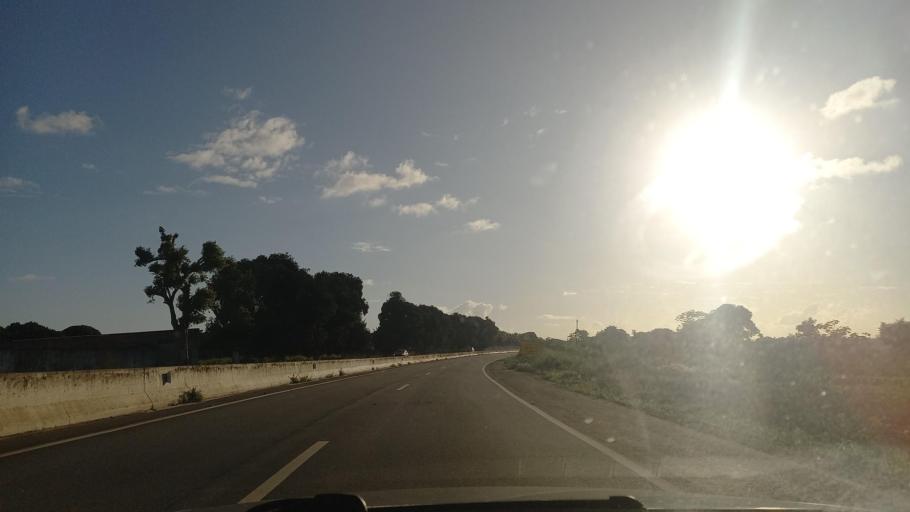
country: BR
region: Alagoas
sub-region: Campo Alegre
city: Campo Alegre
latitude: -9.8036
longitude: -36.2691
